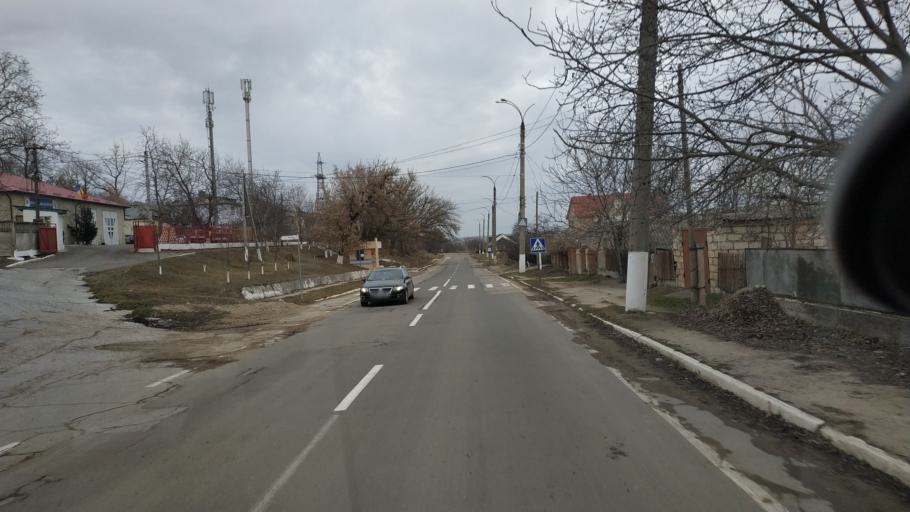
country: MD
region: Criuleni
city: Criuleni
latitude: 47.2220
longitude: 29.1632
